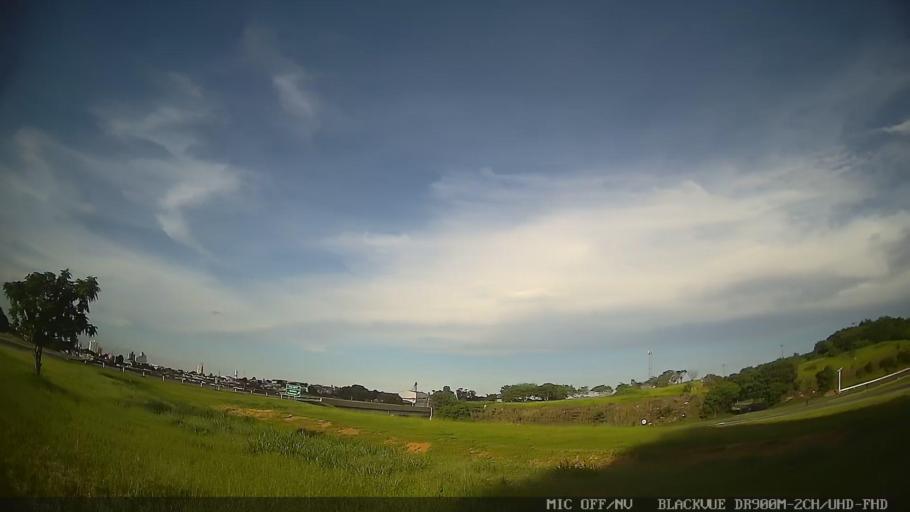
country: BR
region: Sao Paulo
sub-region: Tiete
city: Tiete
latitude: -23.1191
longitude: -47.7189
